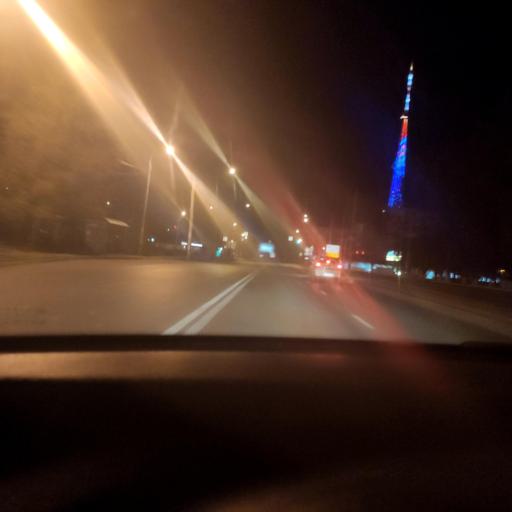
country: RU
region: Samara
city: Samara
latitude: 53.2270
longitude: 50.1959
